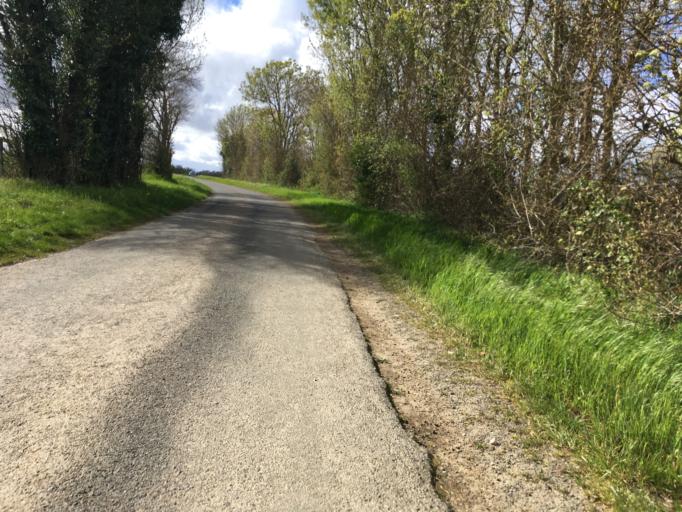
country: FR
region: Poitou-Charentes
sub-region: Departement de la Charente-Maritime
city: Le Thou
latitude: 46.1294
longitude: -0.8636
